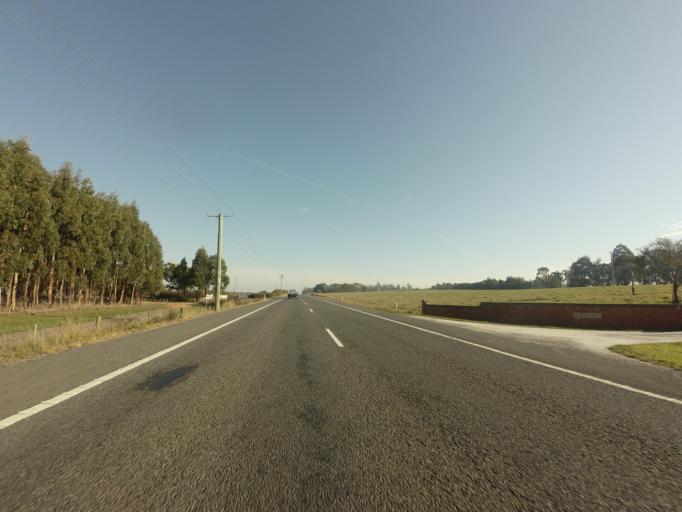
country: AU
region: Tasmania
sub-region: Northern Midlands
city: Longford
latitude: -41.5678
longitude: 147.0870
